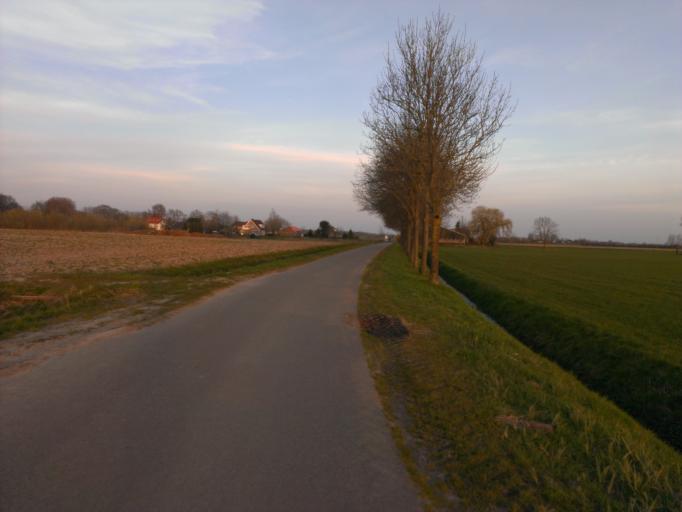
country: NL
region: Overijssel
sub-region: Gemeente Olst-Wijhe
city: Wijhe
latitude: 52.3985
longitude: 6.1004
